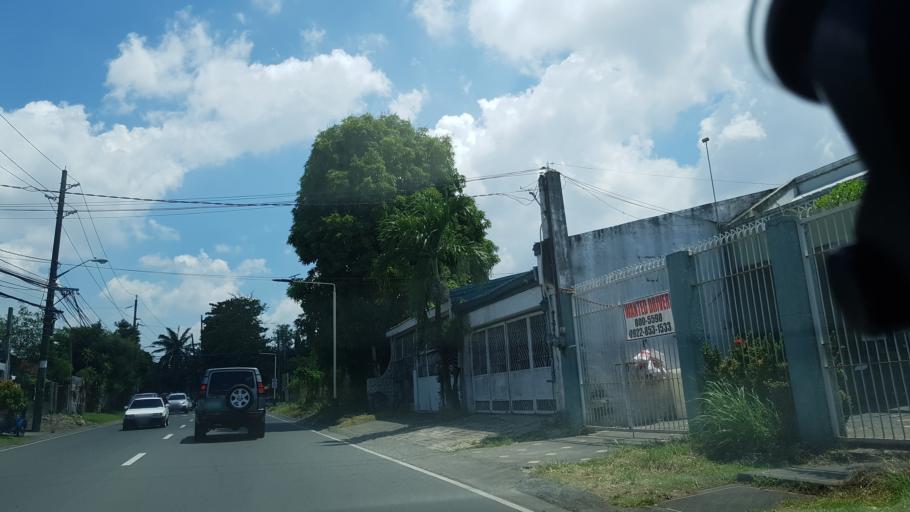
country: PH
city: Sambayanihan People's Village
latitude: 14.4513
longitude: 120.9990
